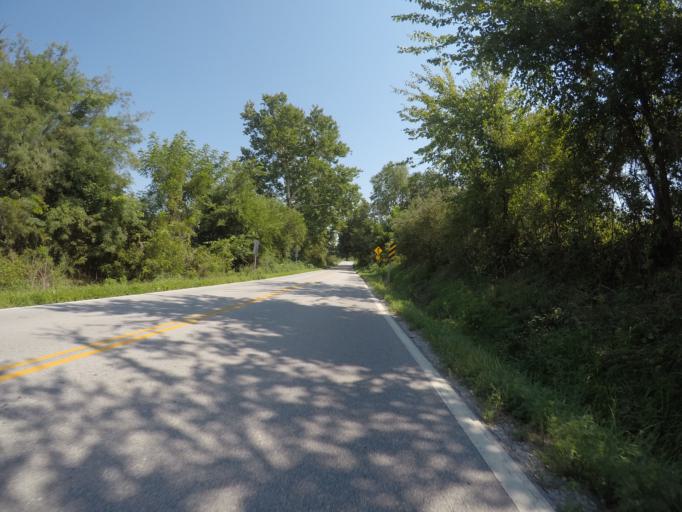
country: US
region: Kansas
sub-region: Leavenworth County
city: Lansing
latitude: 39.2059
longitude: -94.8321
